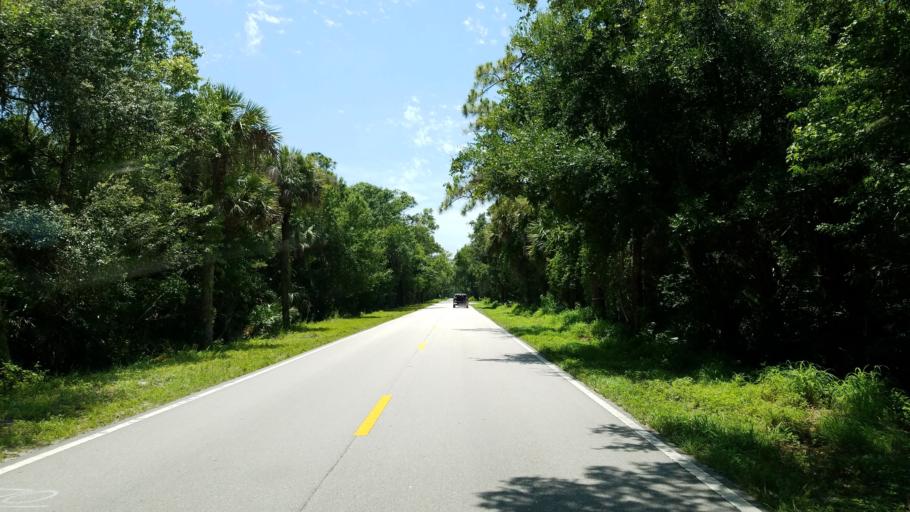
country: US
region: Florida
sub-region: Martin County
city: Indiantown
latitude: 27.1621
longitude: -80.5632
